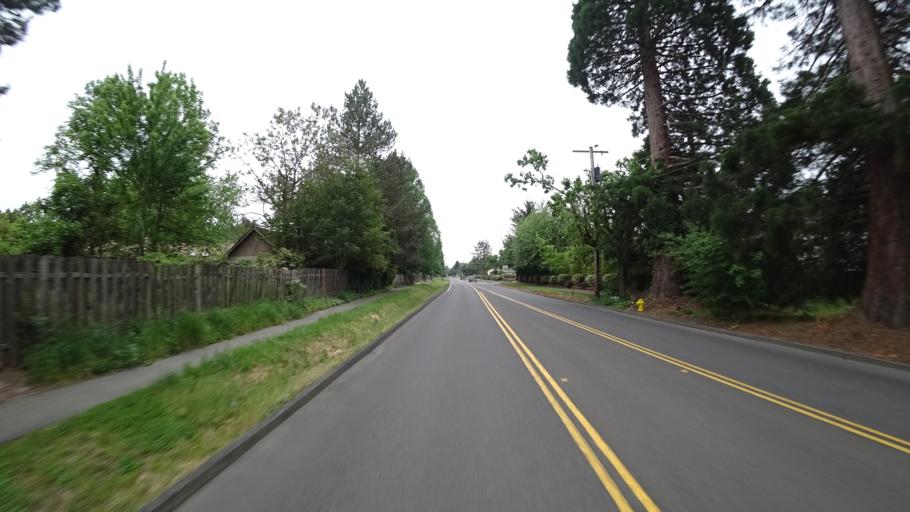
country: US
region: Oregon
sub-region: Washington County
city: Bethany
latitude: 45.5478
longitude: -122.8560
